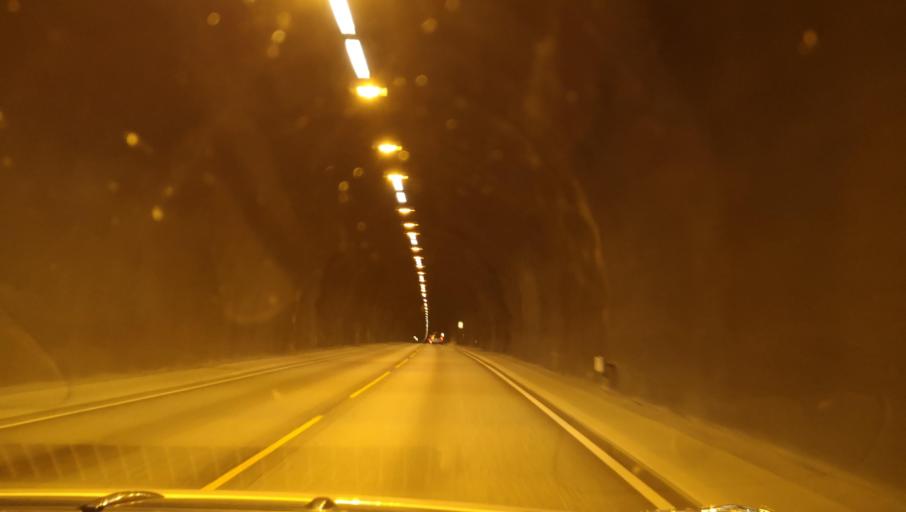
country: NO
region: Hordaland
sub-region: Granvin
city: Granvin
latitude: 60.5841
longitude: 6.6165
